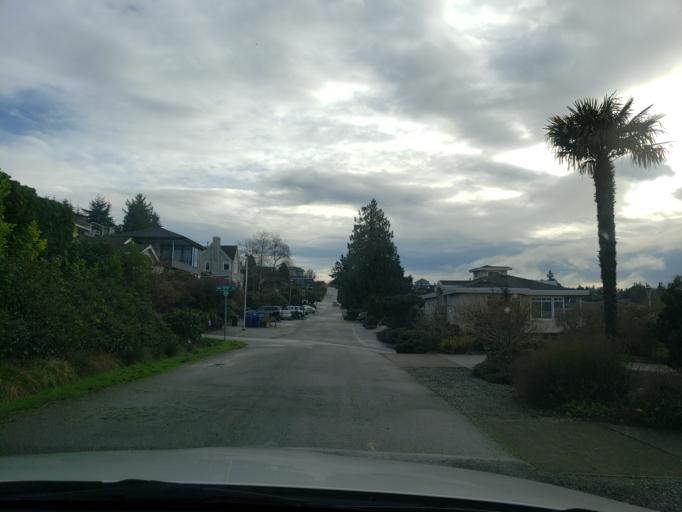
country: US
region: Washington
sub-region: King County
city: Shoreline
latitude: 47.7015
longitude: -122.3853
